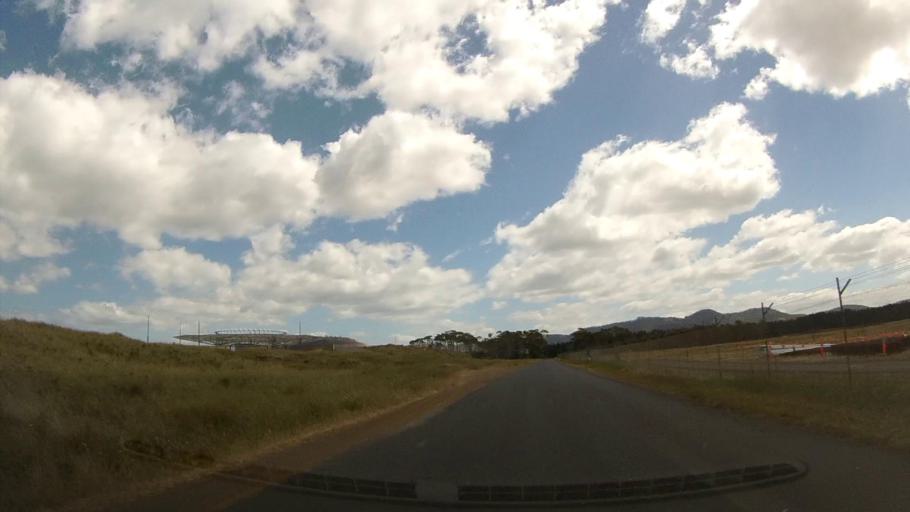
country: AU
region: Tasmania
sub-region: Clarence
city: Seven Mile Beach
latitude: -42.8463
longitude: 147.5269
